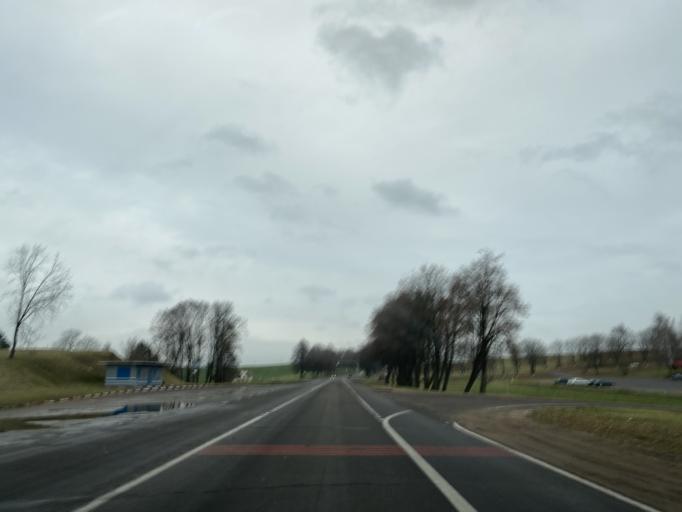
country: BY
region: Minsk
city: Horad Smalyavichy
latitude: 54.0458
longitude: 28.0651
